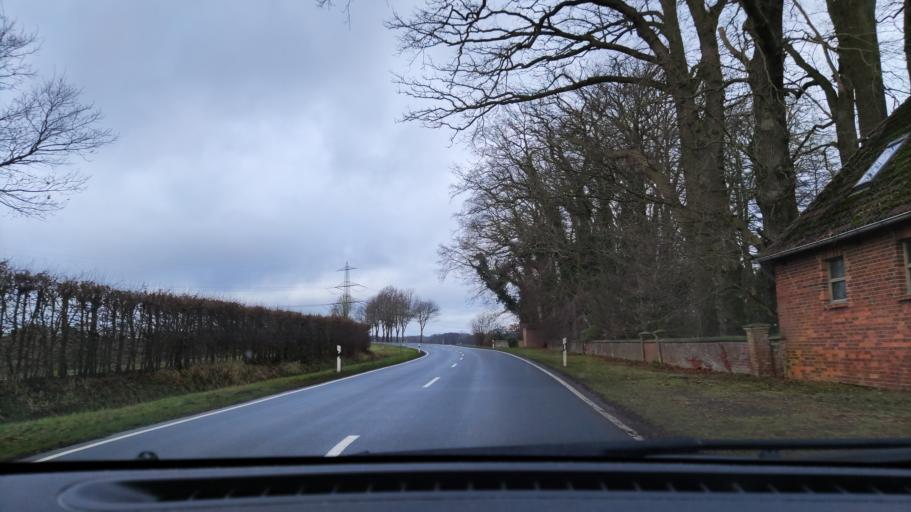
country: DE
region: Lower Saxony
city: Ebstorf
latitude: 53.0360
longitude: 10.3965
